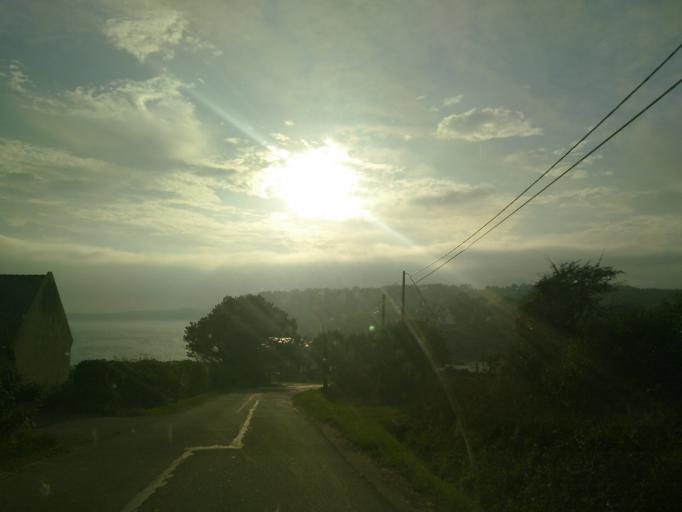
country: FR
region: Brittany
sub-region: Departement du Finistere
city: Crozon
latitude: 48.2379
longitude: -4.4599
